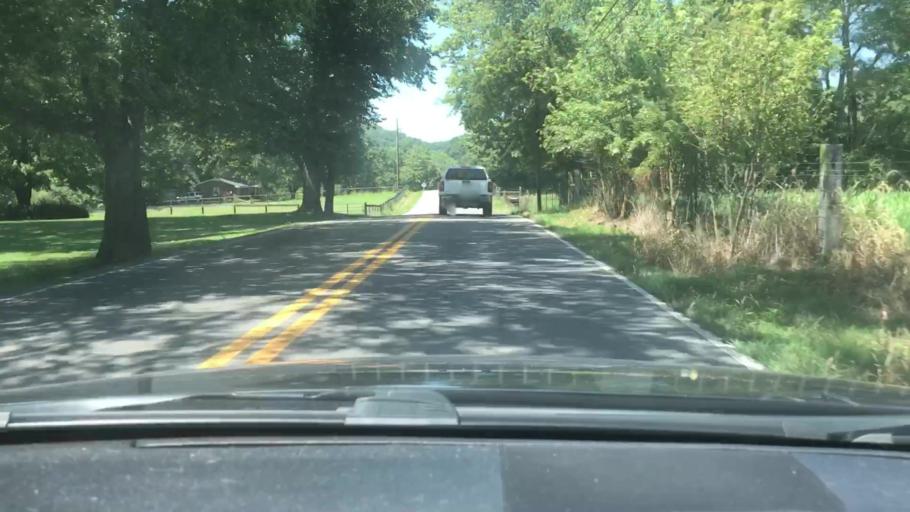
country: US
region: Tennessee
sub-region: Sumner County
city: White House
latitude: 36.4569
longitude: -86.5487
